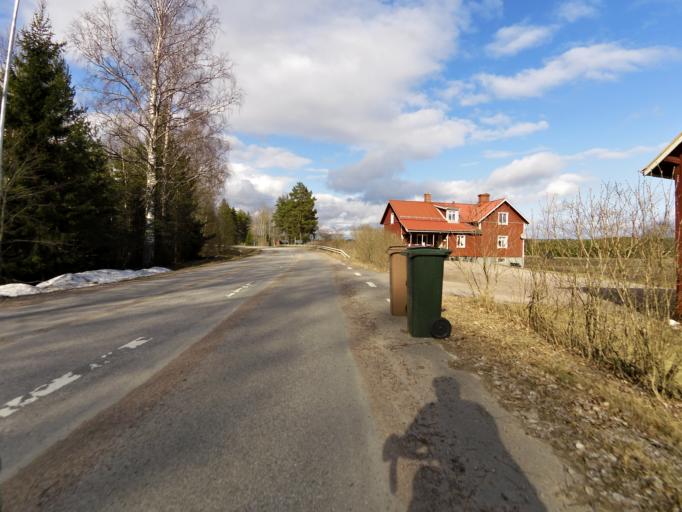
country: SE
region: Dalarna
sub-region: Avesta Kommun
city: Horndal
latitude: 60.4713
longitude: 16.4565
